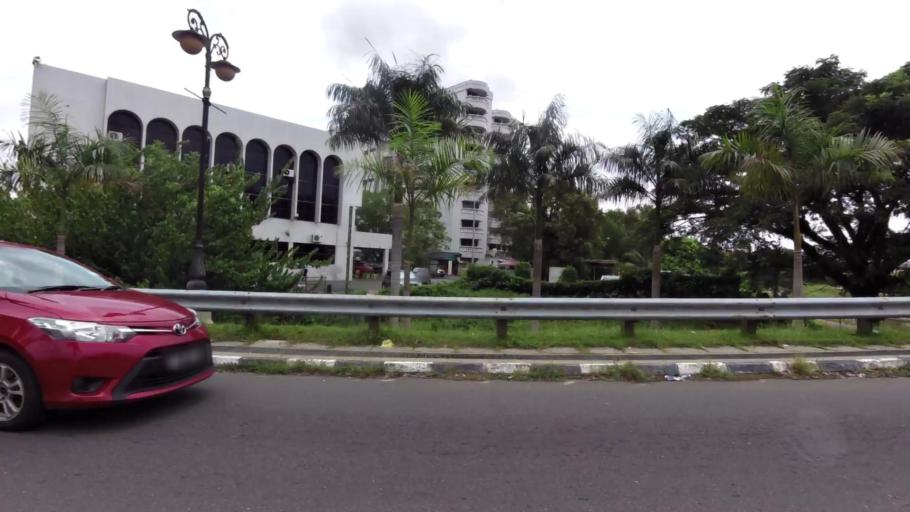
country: BN
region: Brunei and Muara
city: Bandar Seri Begawan
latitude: 4.9057
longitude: 114.9179
